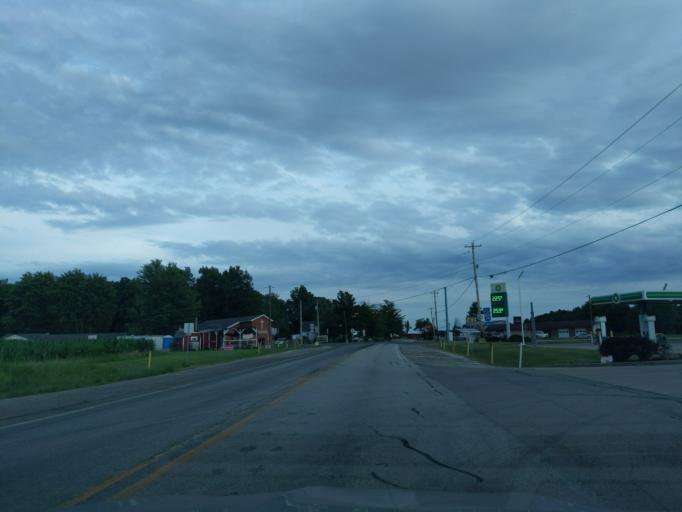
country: US
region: Indiana
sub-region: Ripley County
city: Sunman
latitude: 39.2729
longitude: -85.0976
